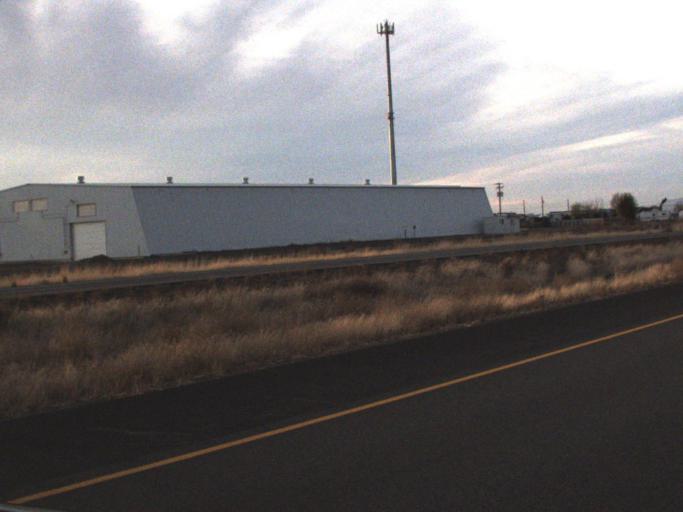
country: US
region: Washington
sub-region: Walla Walla County
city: Burbank
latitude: 46.1814
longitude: -118.9727
